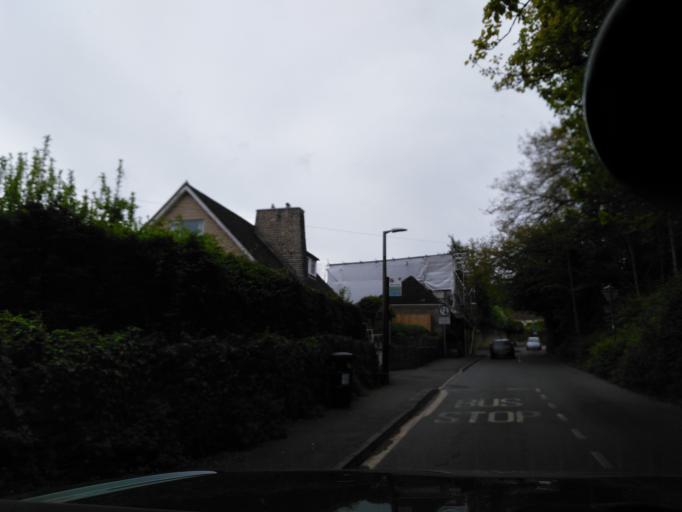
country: GB
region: England
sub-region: Bath and North East Somerset
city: Bath
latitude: 51.3953
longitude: -2.3244
